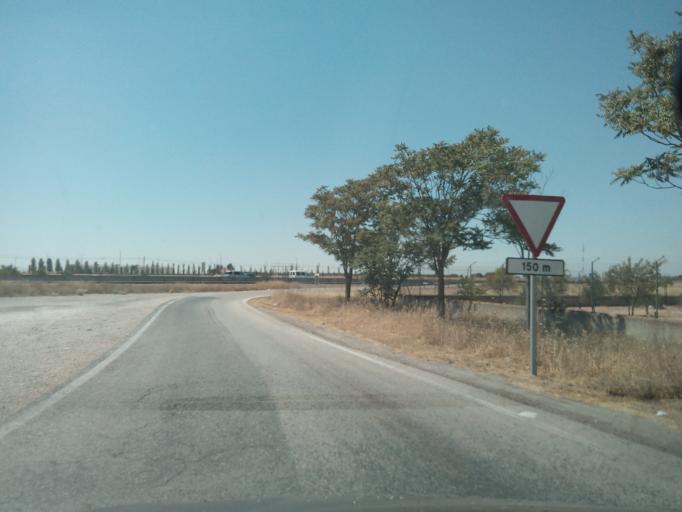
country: ES
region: Castille-La Mancha
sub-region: Province of Toledo
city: Tembleque
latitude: 39.7793
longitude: -3.4784
